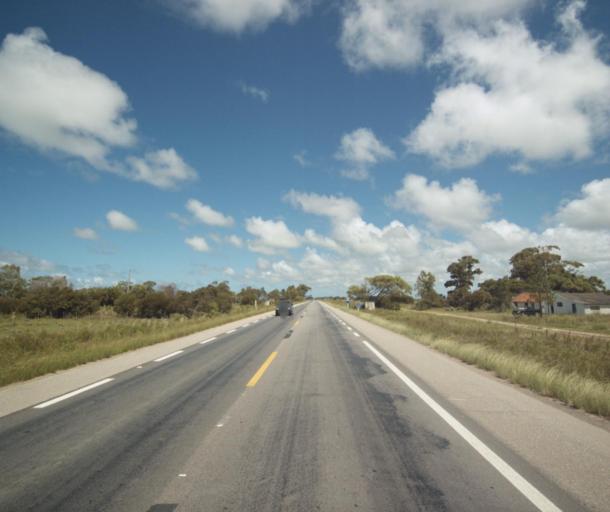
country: BR
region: Rio Grande do Sul
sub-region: Arroio Grande
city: Arroio Grande
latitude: -32.8559
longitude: -52.7051
